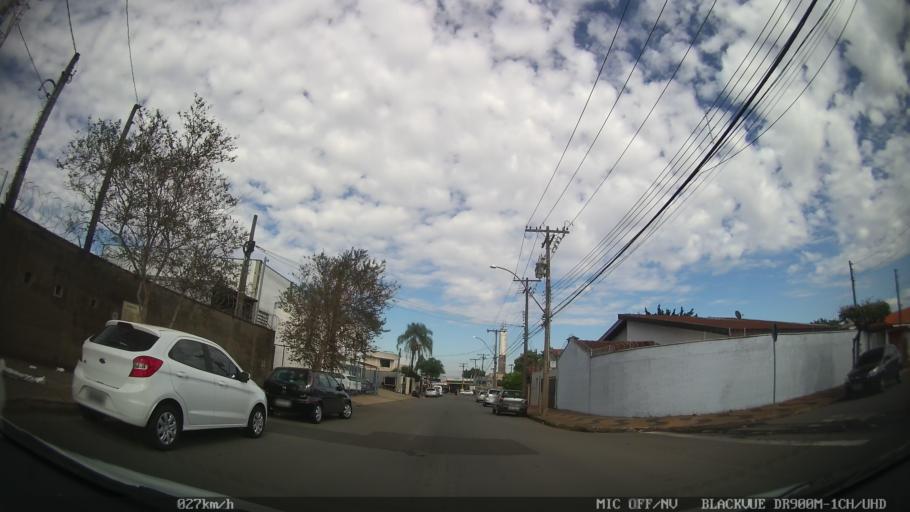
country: BR
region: Sao Paulo
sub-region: Americana
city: Americana
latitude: -22.7428
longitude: -47.3565
